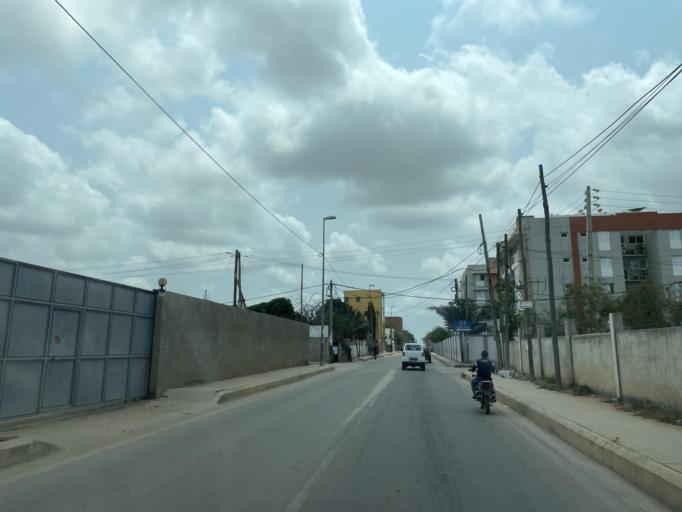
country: AO
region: Luanda
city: Luanda
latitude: -8.9415
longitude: 13.1661
